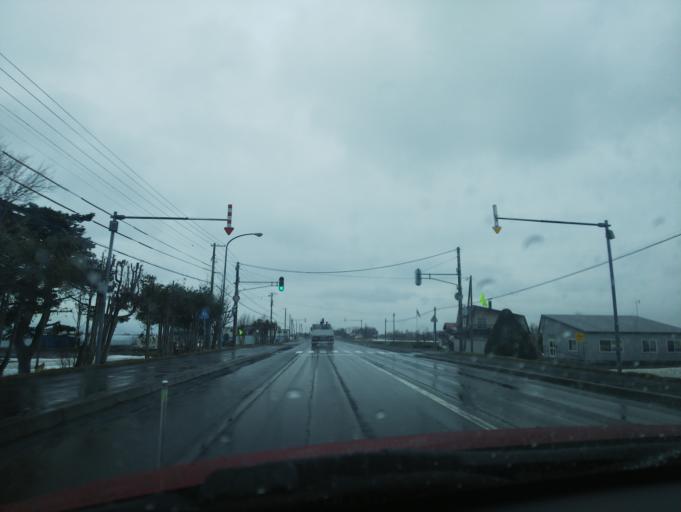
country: JP
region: Hokkaido
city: Nayoro
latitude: 44.2120
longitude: 142.3949
